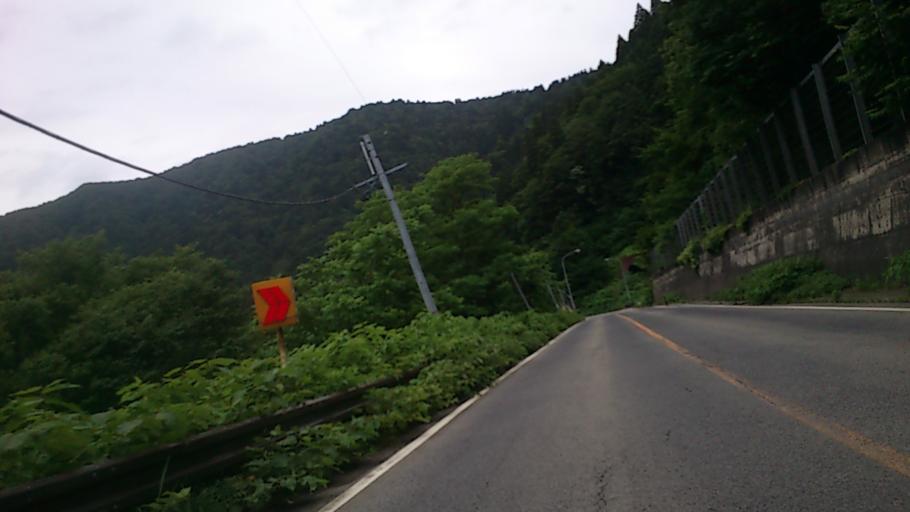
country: JP
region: Yamagata
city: Shinjo
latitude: 38.7512
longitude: 140.0745
